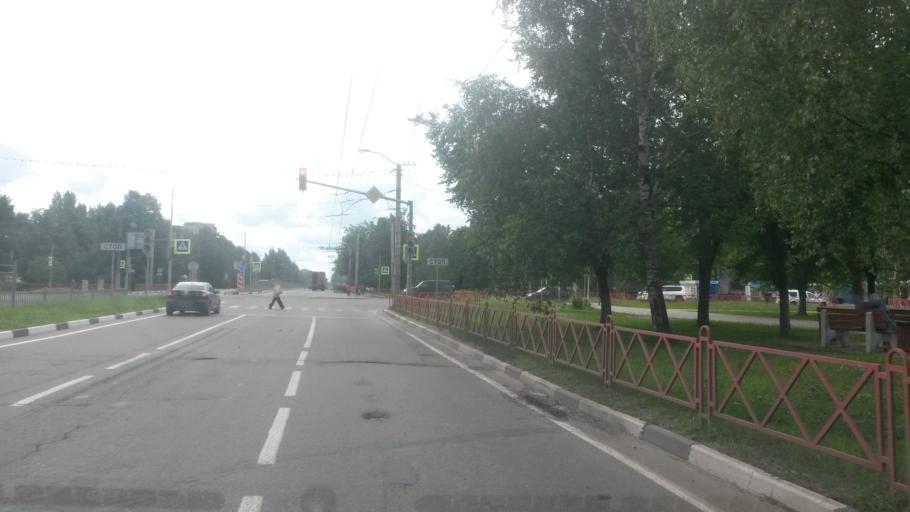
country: RU
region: Jaroslavl
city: Yaroslavl
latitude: 57.6810
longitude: 39.7799
